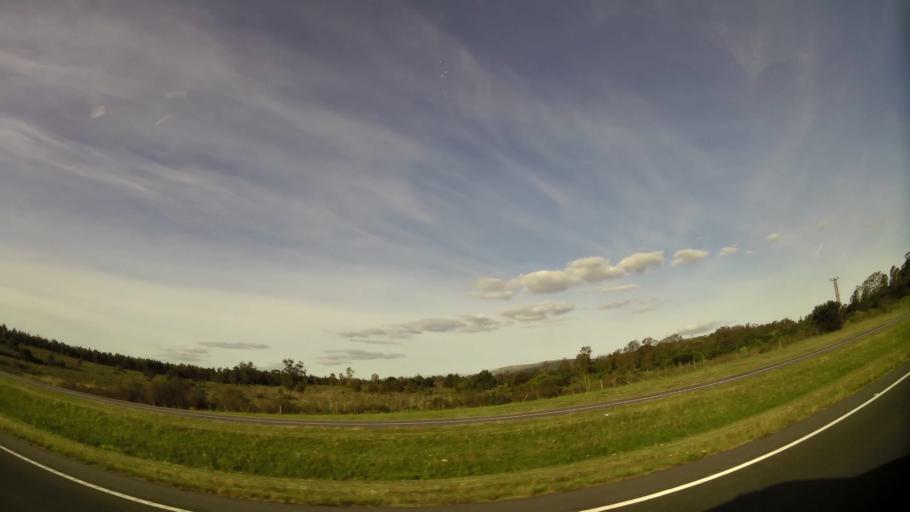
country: UY
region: Maldonado
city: Piriapolis
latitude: -34.7816
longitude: -55.3819
